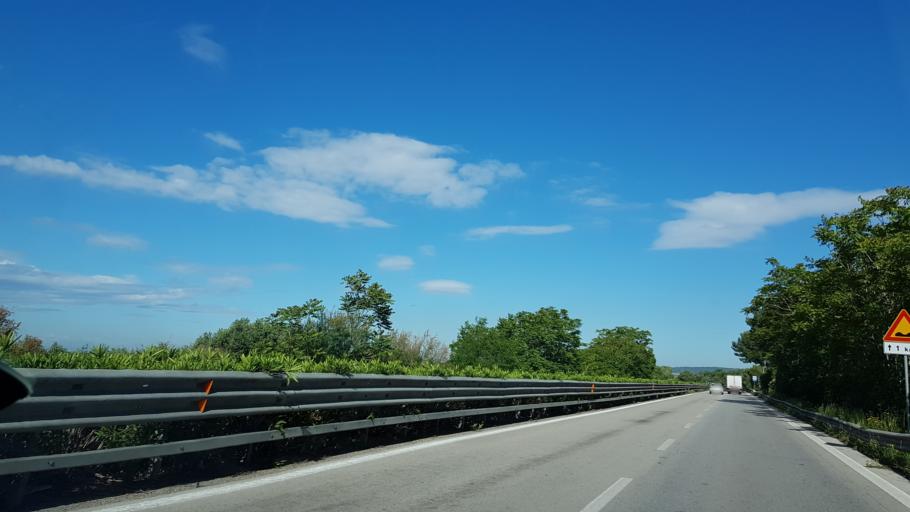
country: IT
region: Apulia
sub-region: Provincia di Taranto
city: Grottaglie
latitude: 40.5293
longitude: 17.4101
